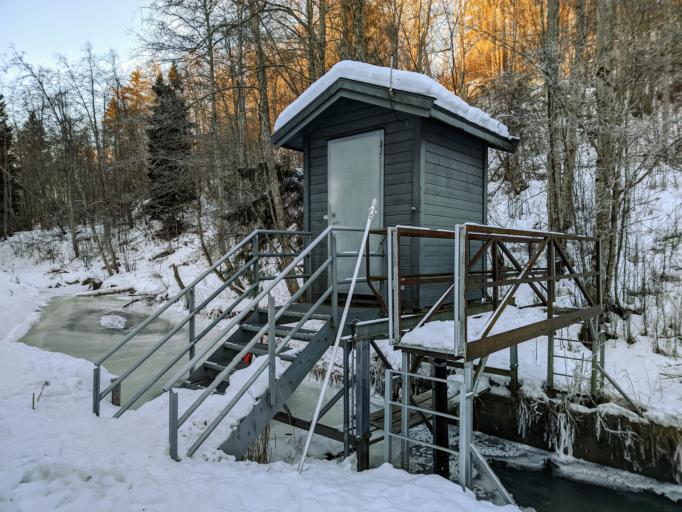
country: NO
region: Akershus
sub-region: Nannestad
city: Teigebyen
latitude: 60.1696
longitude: 11.0636
